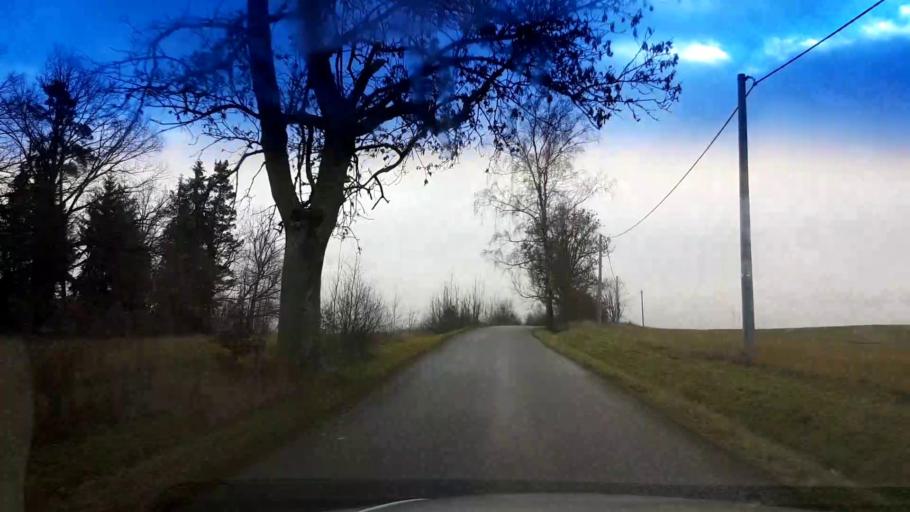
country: CZ
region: Karlovarsky
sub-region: Okres Cheb
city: Cheb
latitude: 50.0436
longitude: 12.3716
